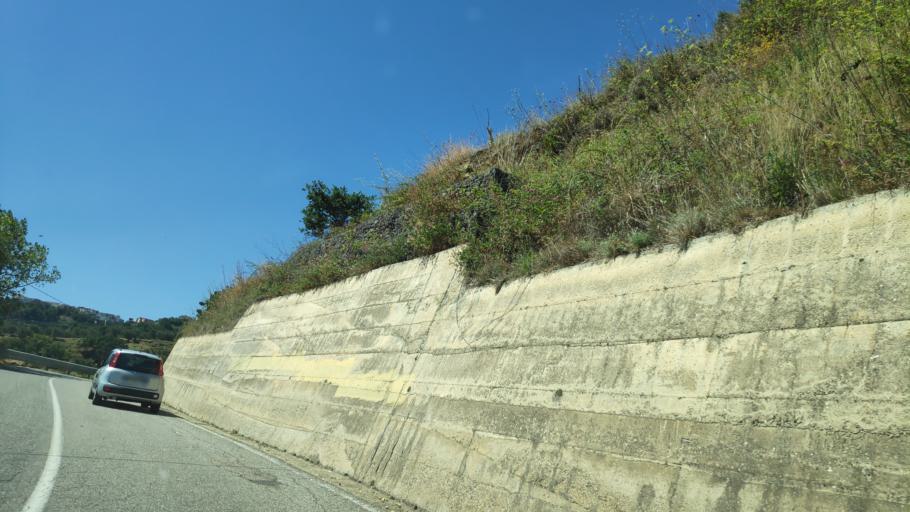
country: IT
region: Calabria
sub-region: Provincia di Catanzaro
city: Montauro
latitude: 38.7470
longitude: 16.5162
